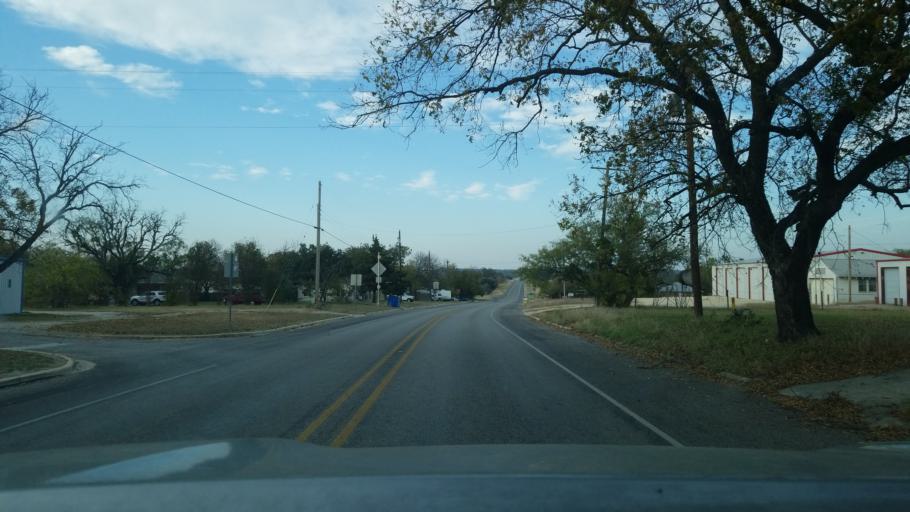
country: US
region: Texas
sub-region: Brown County
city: Lake Brownwood
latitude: 31.9806
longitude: -98.9206
